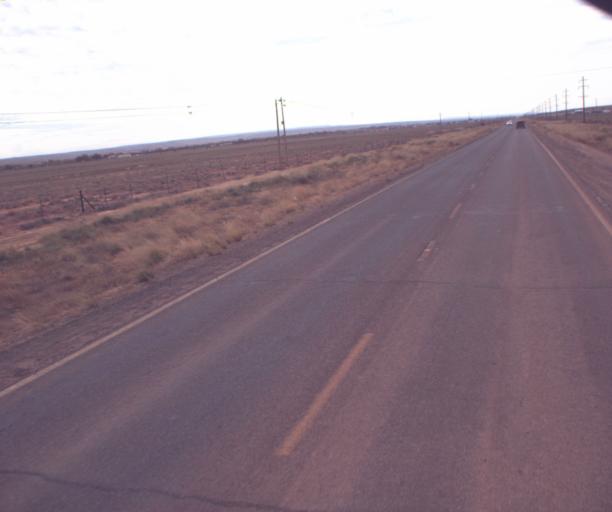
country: US
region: Arizona
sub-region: Apache County
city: Chinle
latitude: 36.2076
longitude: -109.6001
